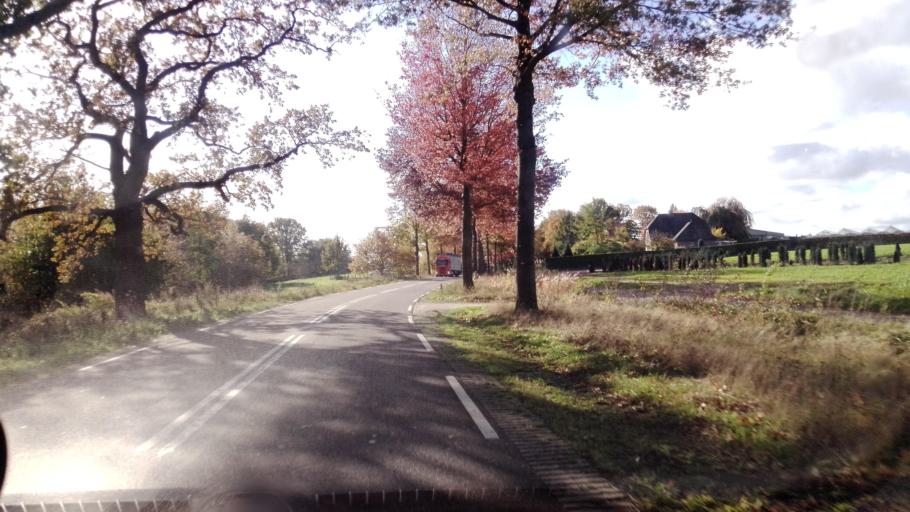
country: NL
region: Limburg
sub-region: Gemeente Venlo
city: Arcen
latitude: 51.4501
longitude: 6.1531
